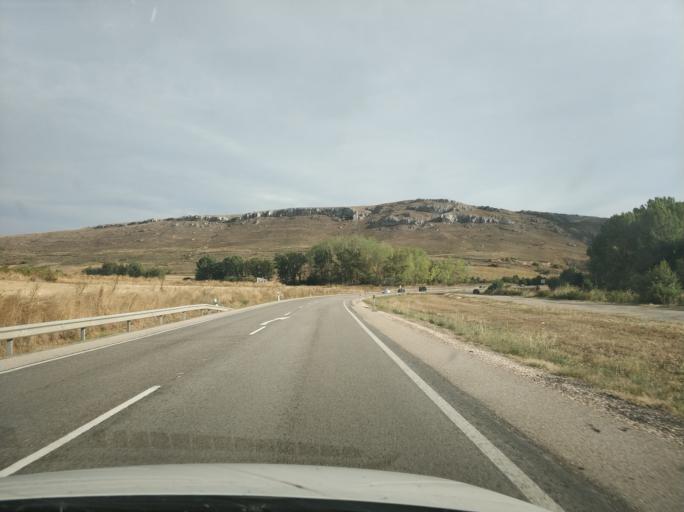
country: ES
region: Castille and Leon
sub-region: Provincia de Burgos
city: Quintanaortuno
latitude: 42.4962
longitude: -3.6960
